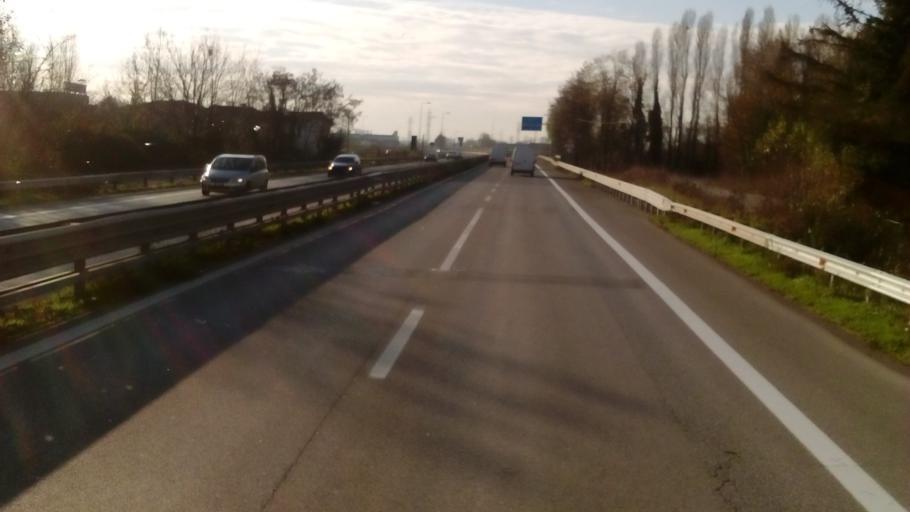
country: IT
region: Veneto
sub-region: Provincia di Venezia
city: Mestre
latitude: 45.4635
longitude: 12.2107
